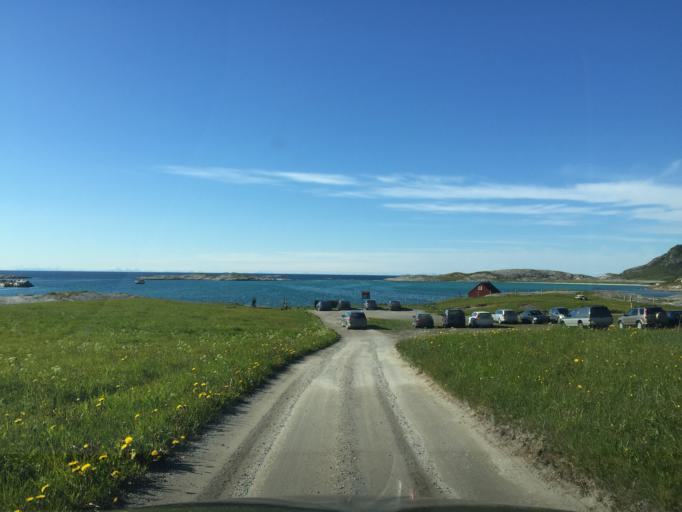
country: NO
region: Nordland
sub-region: Bodo
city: Loding
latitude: 67.4108
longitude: 14.6285
